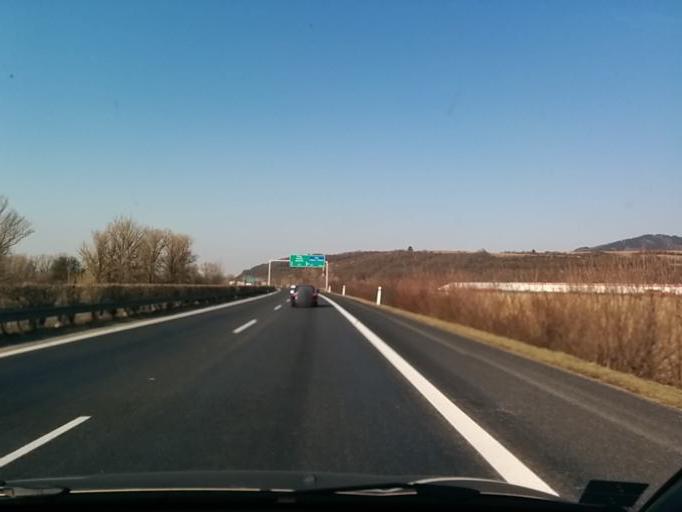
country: SK
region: Trnavsky
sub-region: Okres Trnava
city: Piestany
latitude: 48.6629
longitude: 17.8699
